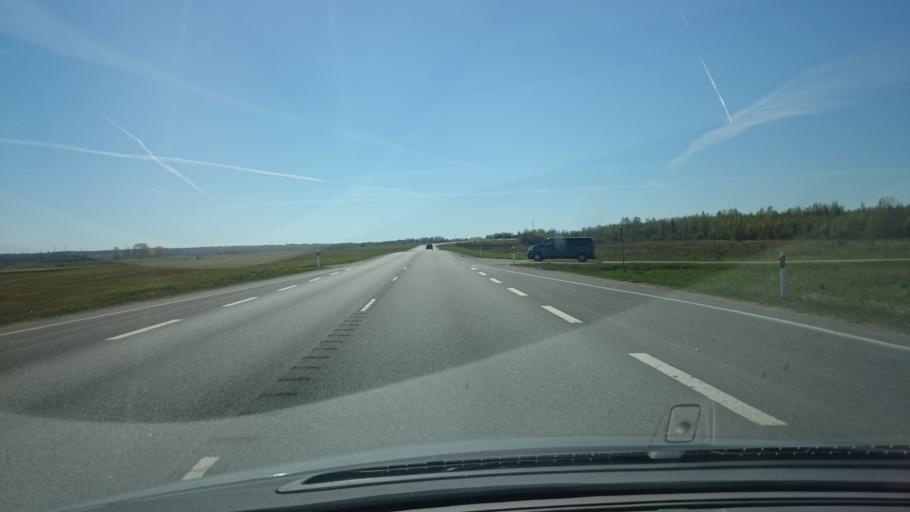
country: EE
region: Ida-Virumaa
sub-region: Narva-Joesuu linn
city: Narva-Joesuu
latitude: 59.3987
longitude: 28.0077
